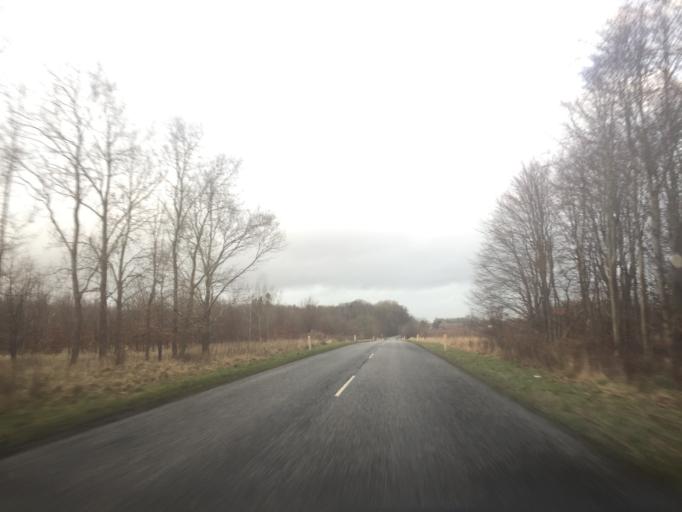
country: DK
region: Capital Region
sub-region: Egedal Kommune
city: Smorumnedre
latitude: 55.6953
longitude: 12.3229
